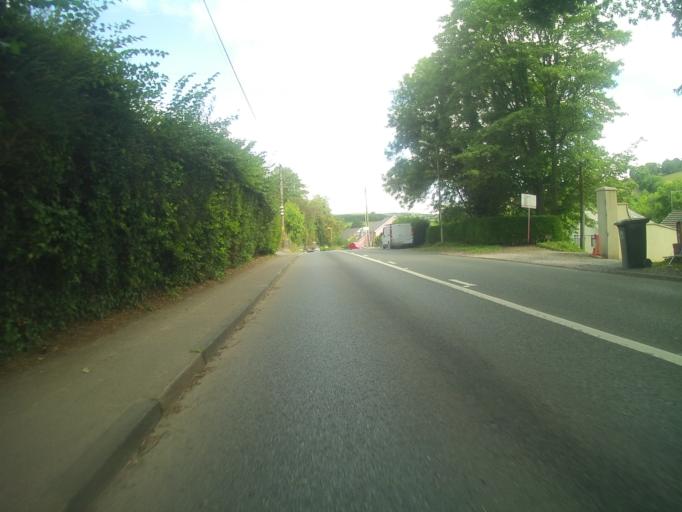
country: GB
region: England
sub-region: Devon
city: Buckfastleigh
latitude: 50.4844
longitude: -3.7708
